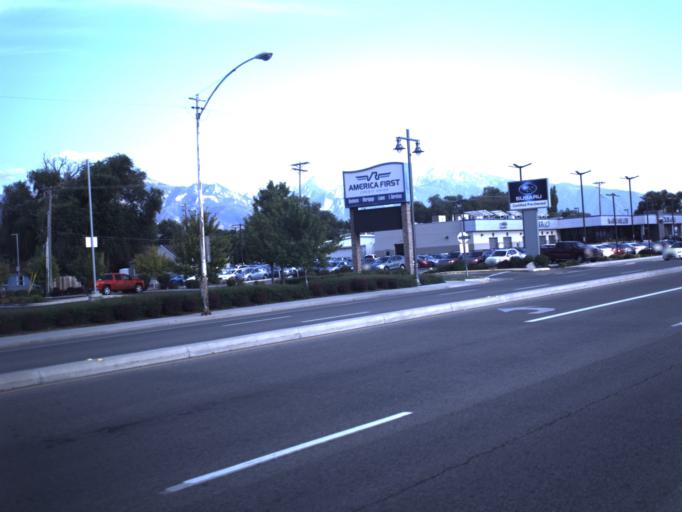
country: US
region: Utah
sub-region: Salt Lake County
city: Centerfield
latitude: 40.6953
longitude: -111.8884
